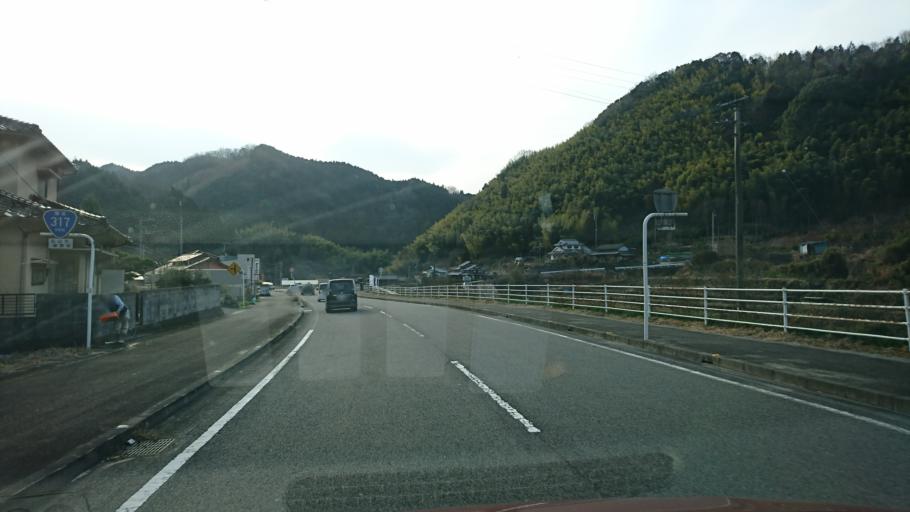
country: JP
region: Ehime
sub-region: Shikoku-chuo Shi
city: Matsuyama
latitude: 33.8985
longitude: 132.8623
